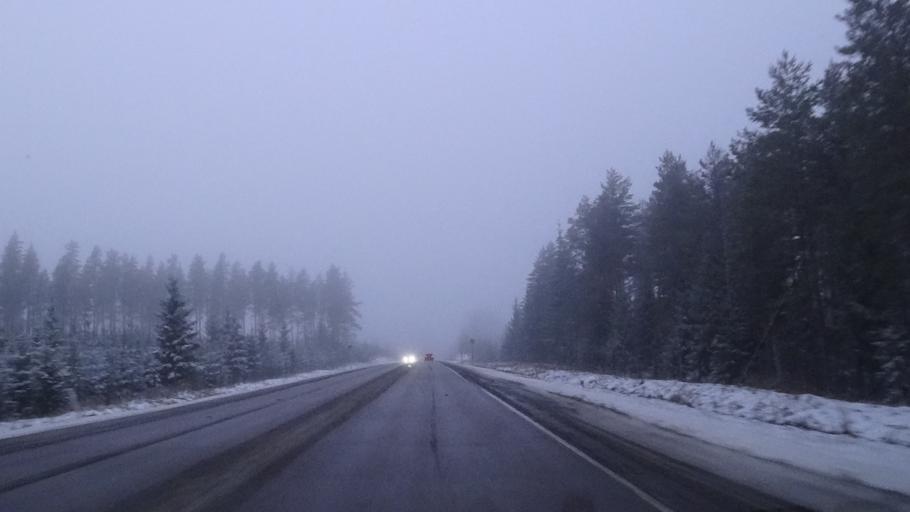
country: FI
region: Paijanne Tavastia
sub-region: Lahti
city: Hollola
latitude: 60.9898
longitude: 25.3870
